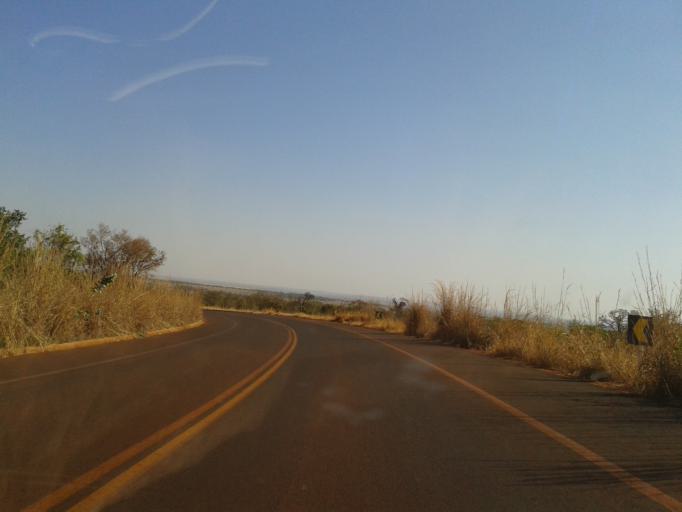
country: BR
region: Minas Gerais
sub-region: Ituiutaba
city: Ituiutaba
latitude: -19.0285
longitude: -49.5028
